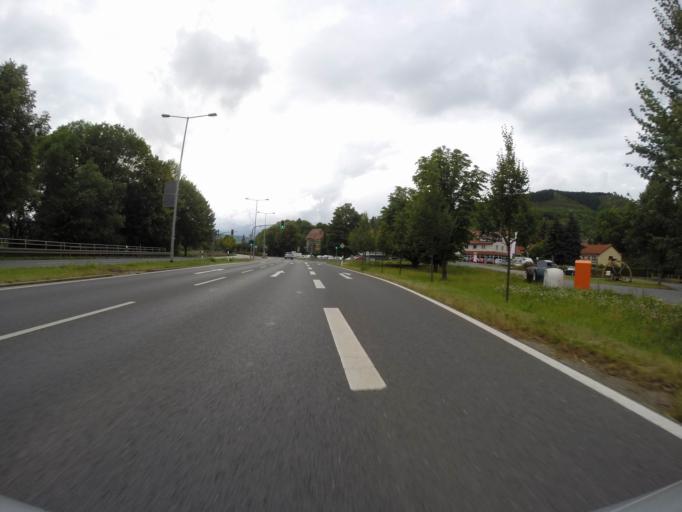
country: DE
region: Thuringia
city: Jena
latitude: 50.9023
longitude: 11.5985
